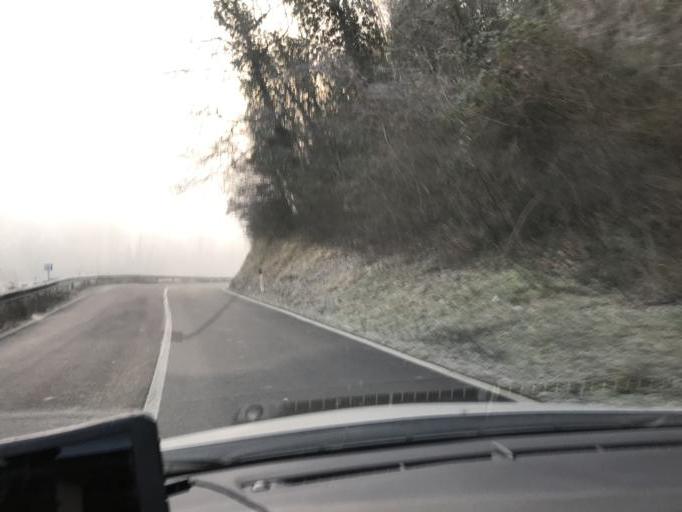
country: IT
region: Latium
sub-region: Provincia di Rieti
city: Colli sul Velino
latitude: 42.5186
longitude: 12.7360
